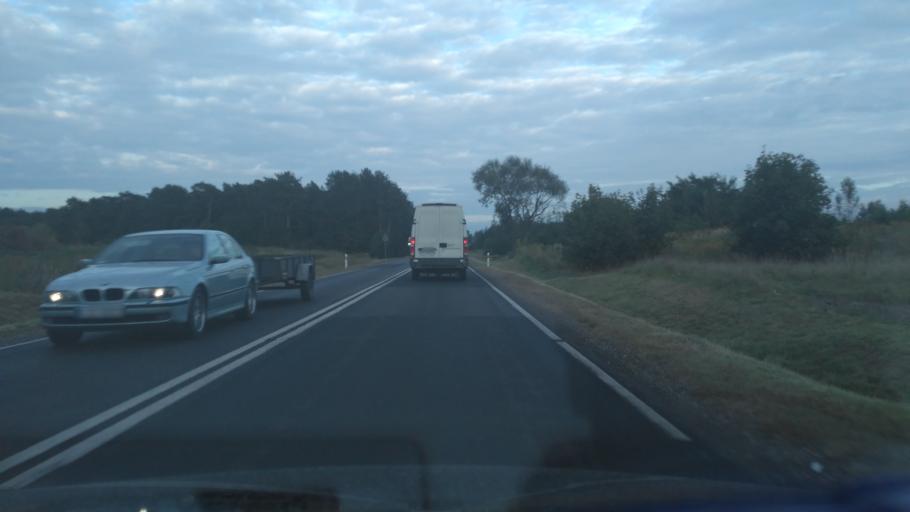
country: PL
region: Lublin Voivodeship
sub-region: Powiat leczynski
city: Spiczyn
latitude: 51.3012
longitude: 22.7487
